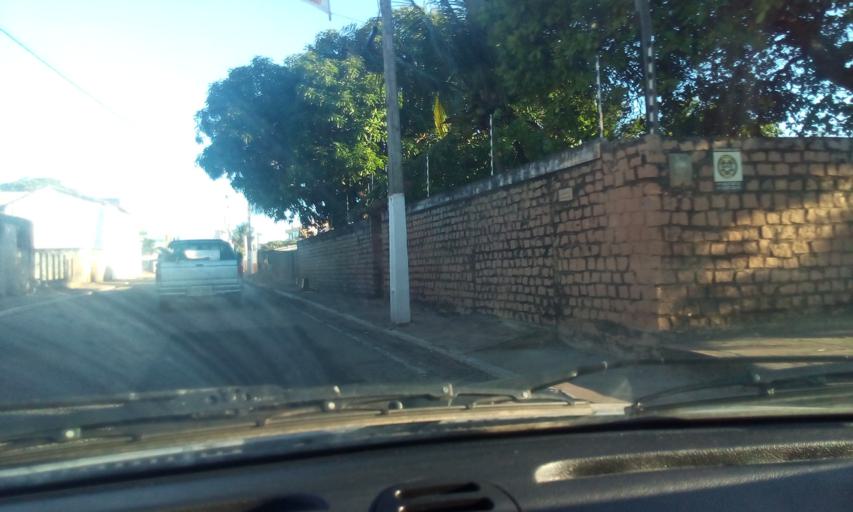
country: BR
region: Rio Grande do Norte
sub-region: Parnamirim
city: Parnamirim
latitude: -5.9620
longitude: -35.1486
